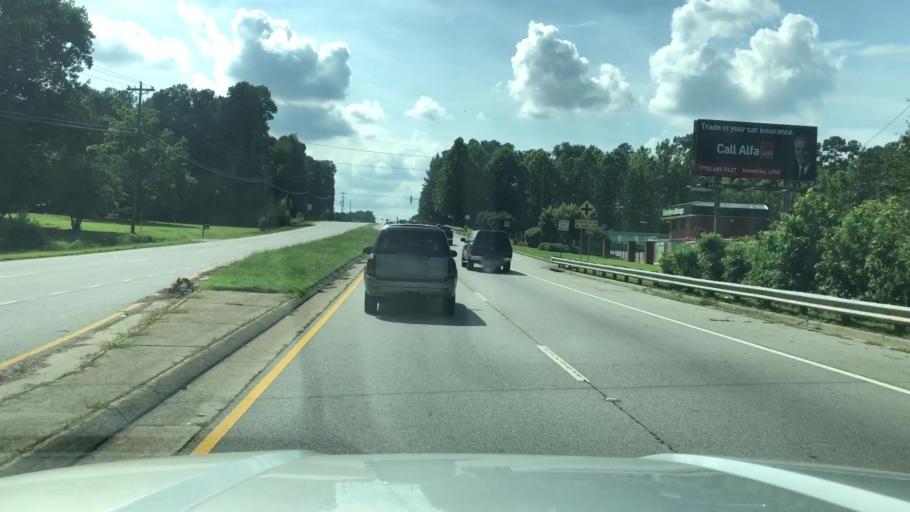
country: US
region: Georgia
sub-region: Douglas County
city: Lithia Springs
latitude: 33.7403
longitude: -84.6782
